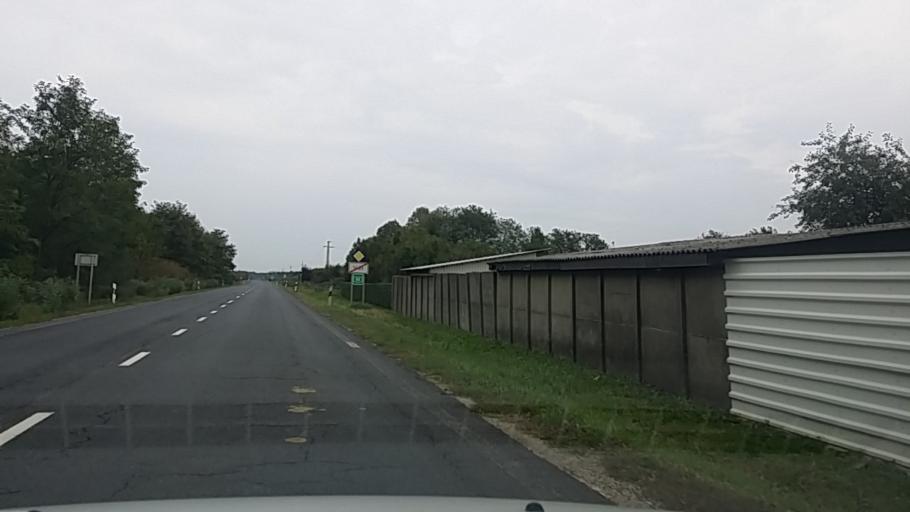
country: HU
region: Vas
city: Vep
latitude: 47.2836
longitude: 16.7810
